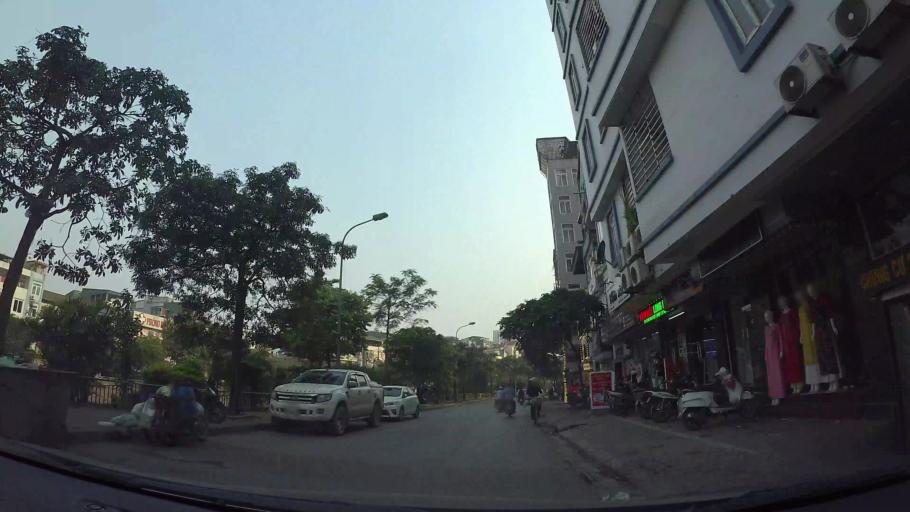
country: VN
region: Ha Noi
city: Thanh Xuan
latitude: 21.0006
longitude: 105.8181
